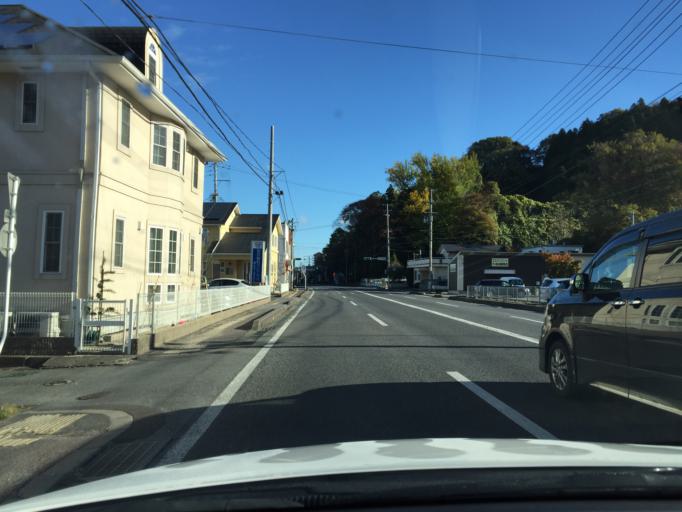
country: JP
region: Fukushima
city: Iwaki
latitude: 37.0433
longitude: 140.8682
